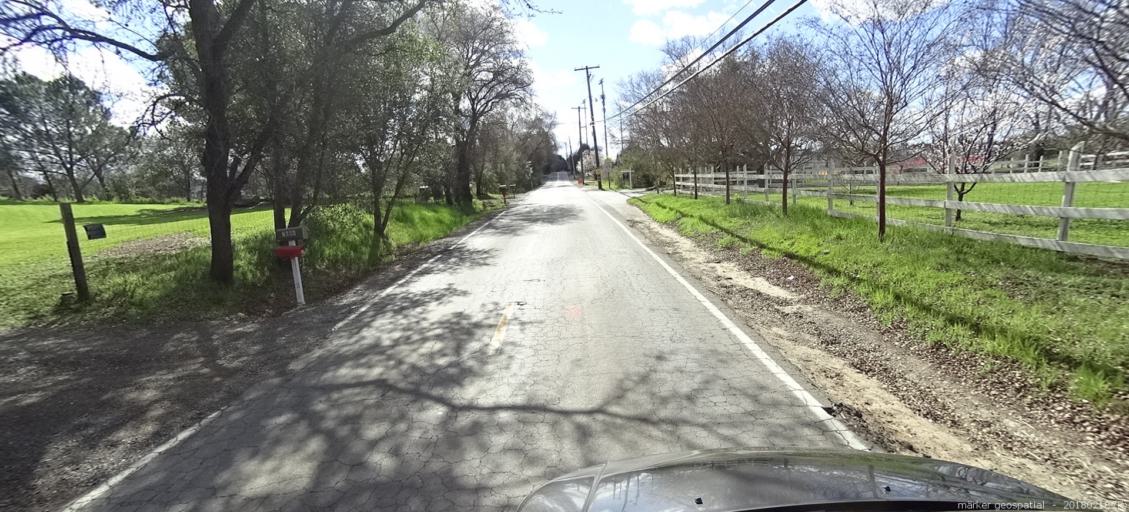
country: US
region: California
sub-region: Sacramento County
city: Orangevale
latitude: 38.7042
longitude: -121.2113
